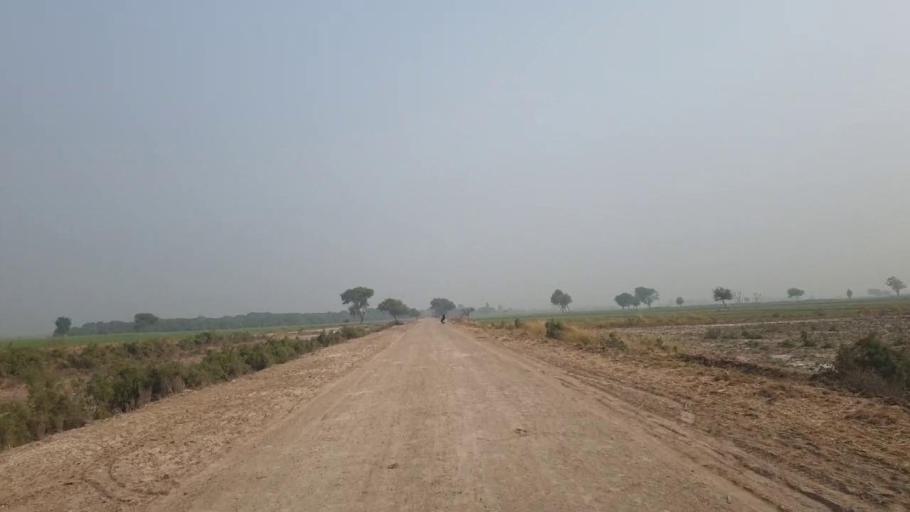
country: PK
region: Sindh
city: Tando Adam
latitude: 25.8203
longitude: 68.5886
